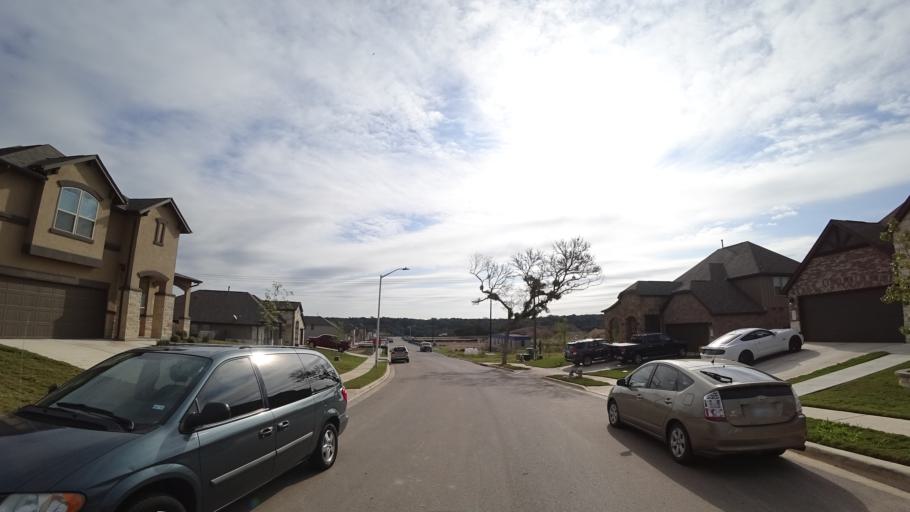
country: US
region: Texas
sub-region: Travis County
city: Manchaca
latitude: 30.1292
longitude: -97.8474
